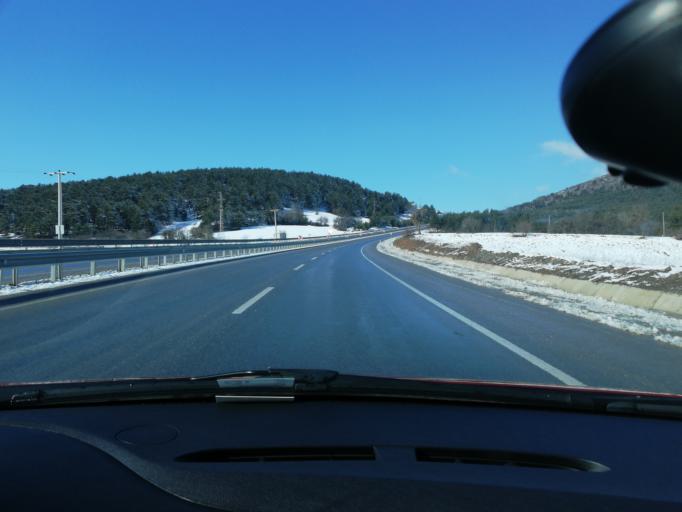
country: TR
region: Kastamonu
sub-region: Cide
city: Kastamonu
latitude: 41.3607
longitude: 33.7076
